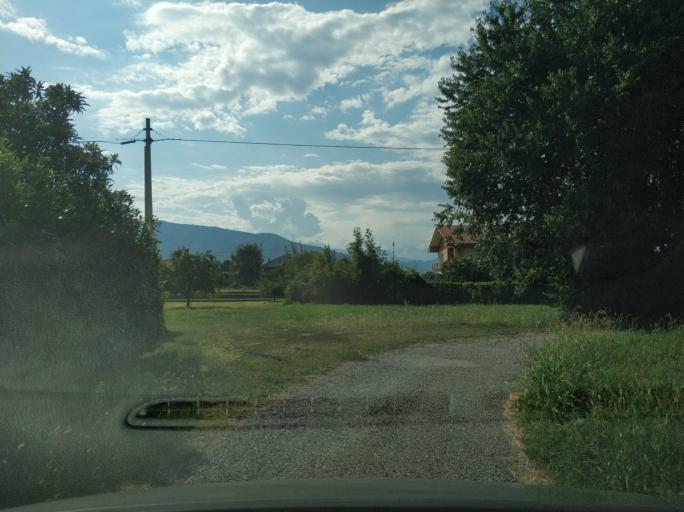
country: IT
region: Piedmont
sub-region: Provincia di Torino
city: Nole
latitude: 45.2485
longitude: 7.5642
